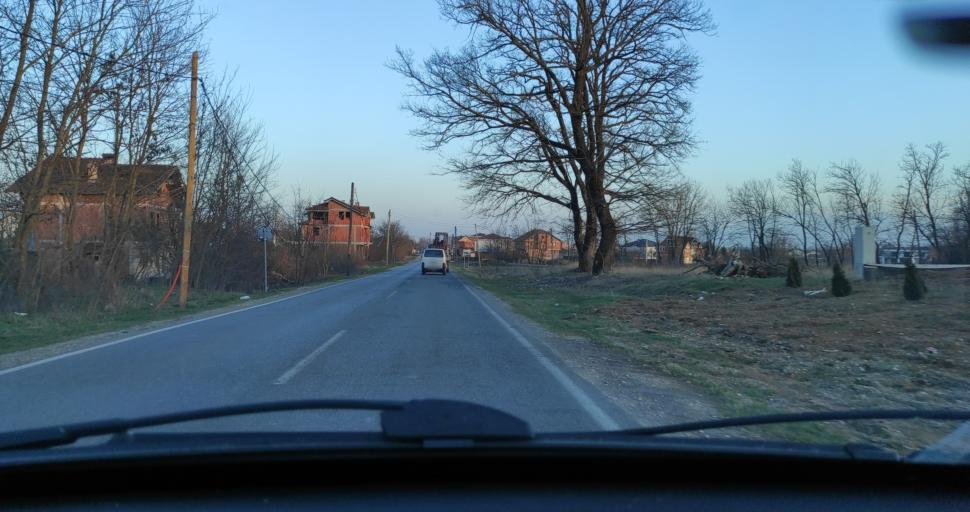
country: XK
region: Gjakova
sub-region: Komuna e Decanit
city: Gllogjan
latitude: 42.4367
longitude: 20.3722
